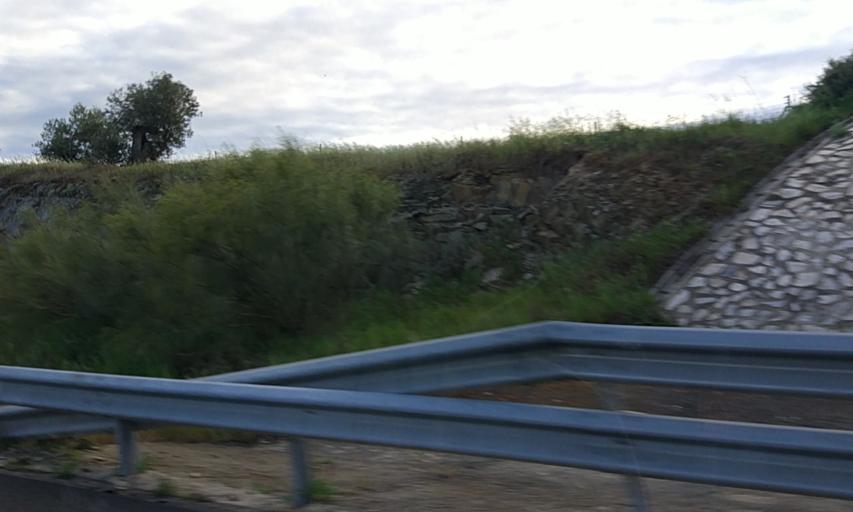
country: ES
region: Extremadura
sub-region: Provincia de Caceres
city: Casar de Caceres
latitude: 39.5617
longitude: -6.4000
